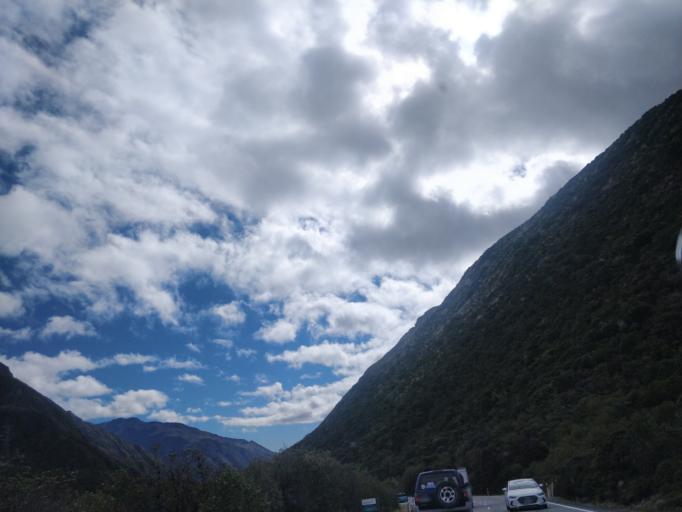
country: NZ
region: West Coast
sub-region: Grey District
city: Greymouth
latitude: -42.9034
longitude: 171.5602
